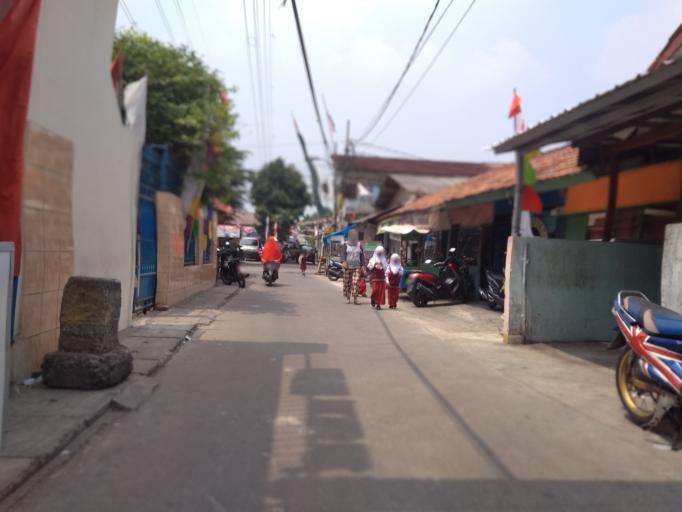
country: ID
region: West Java
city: Pamulang
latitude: -6.3232
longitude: 106.7935
